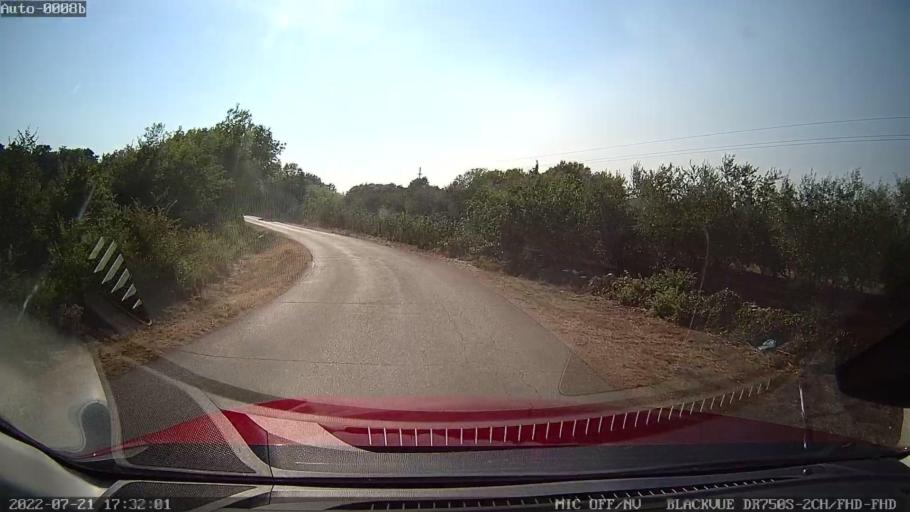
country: HR
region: Istarska
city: Karojba
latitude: 45.1749
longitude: 13.7585
